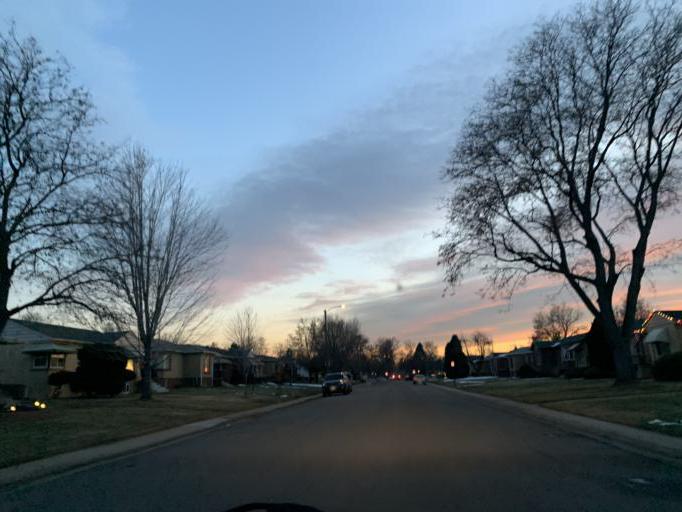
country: US
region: Colorado
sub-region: Adams County
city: Berkley
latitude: 39.7749
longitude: -105.0381
